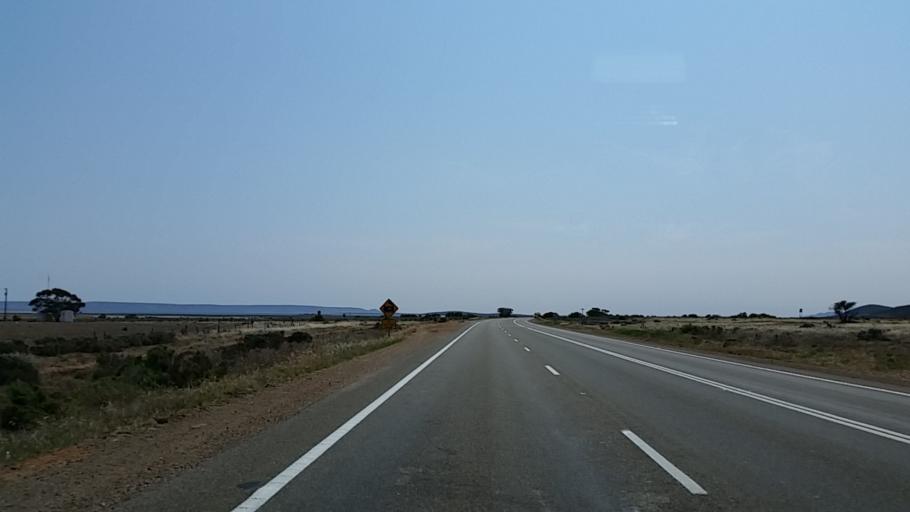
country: AU
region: South Australia
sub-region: Port Augusta
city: Port Augusta
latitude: -32.8070
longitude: 137.9648
